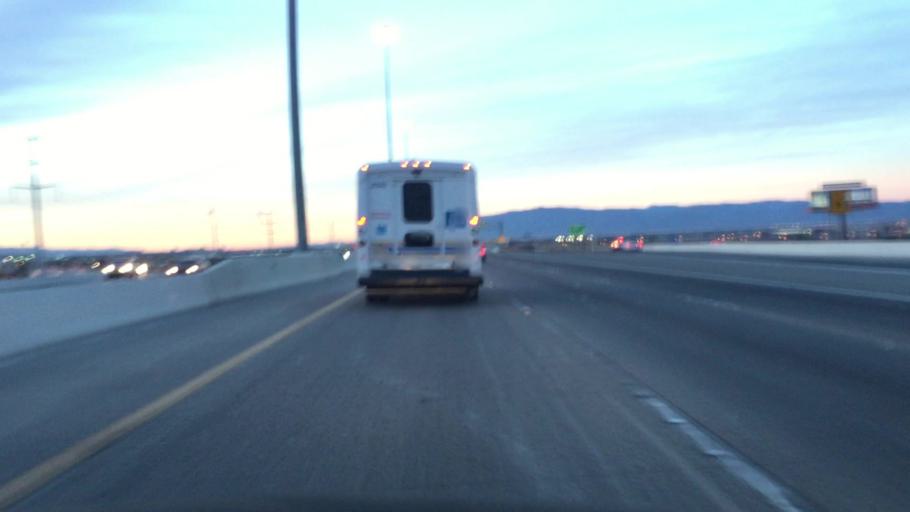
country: US
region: Nevada
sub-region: Clark County
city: Henderson
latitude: 36.0602
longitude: -115.0297
